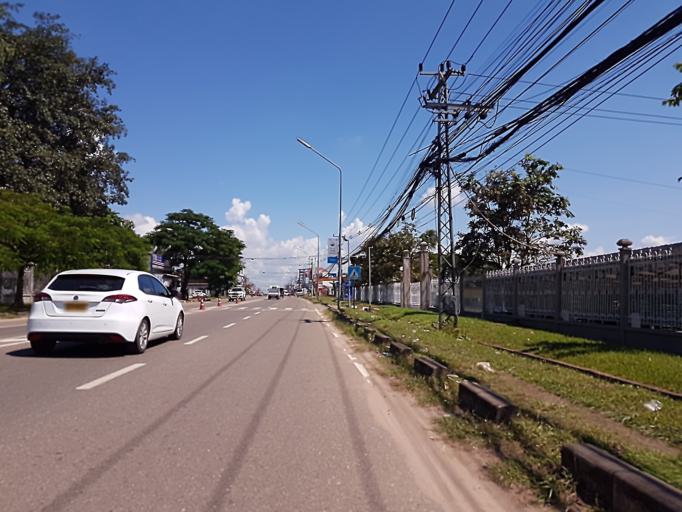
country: TH
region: Nong Khai
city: Si Chiang Mai
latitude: 17.9011
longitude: 102.6326
